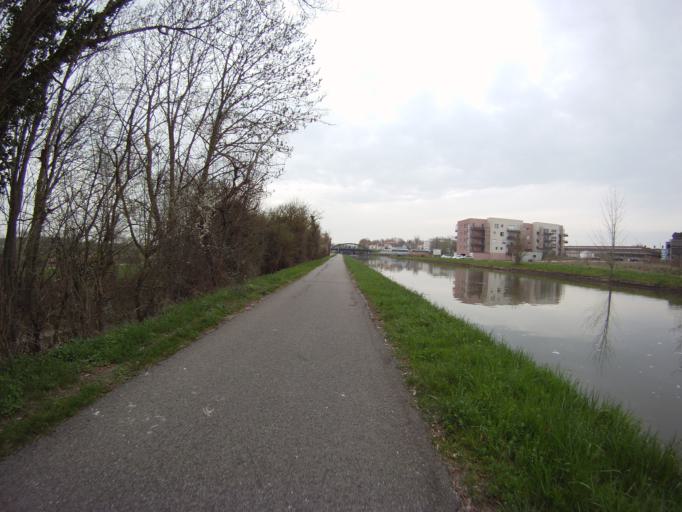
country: FR
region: Lorraine
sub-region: Departement de Meurthe-et-Moselle
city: Laneuveville-devant-Nancy
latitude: 48.6615
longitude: 6.2279
